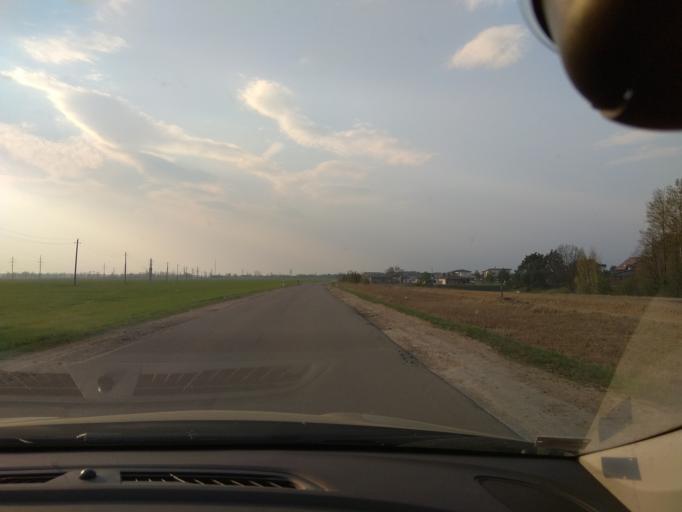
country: LT
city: Baltoji Voke
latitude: 54.6021
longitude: 25.1366
